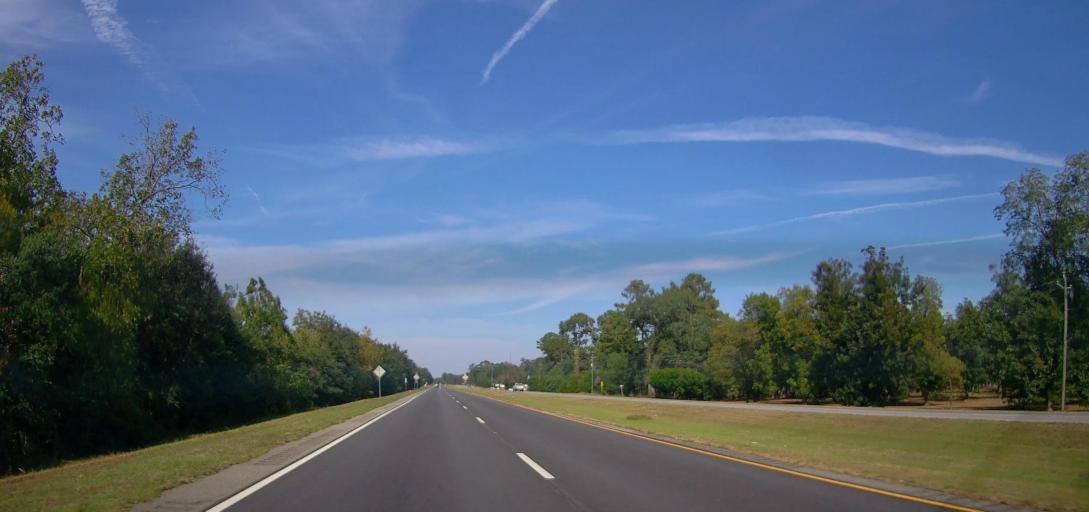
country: US
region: Georgia
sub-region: Dougherty County
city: Putney
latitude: 31.3814
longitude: -84.1498
